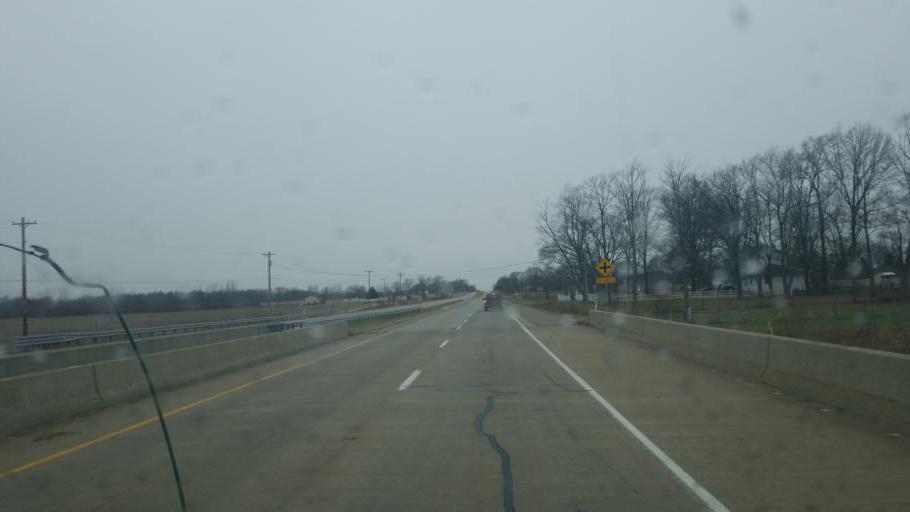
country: US
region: Indiana
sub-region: Hancock County
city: Greenfield
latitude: 39.7889
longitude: -85.6852
